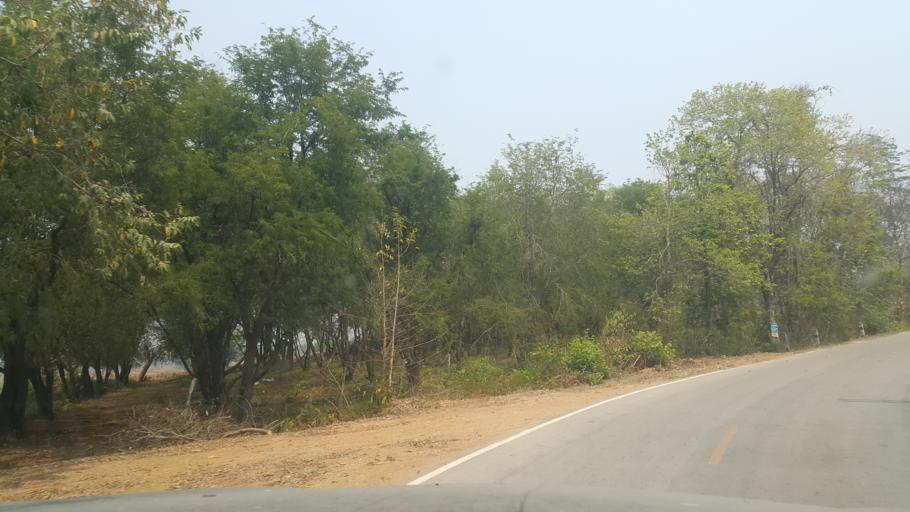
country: TH
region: Lampang
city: Sop Prap
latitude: 17.8950
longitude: 99.3146
